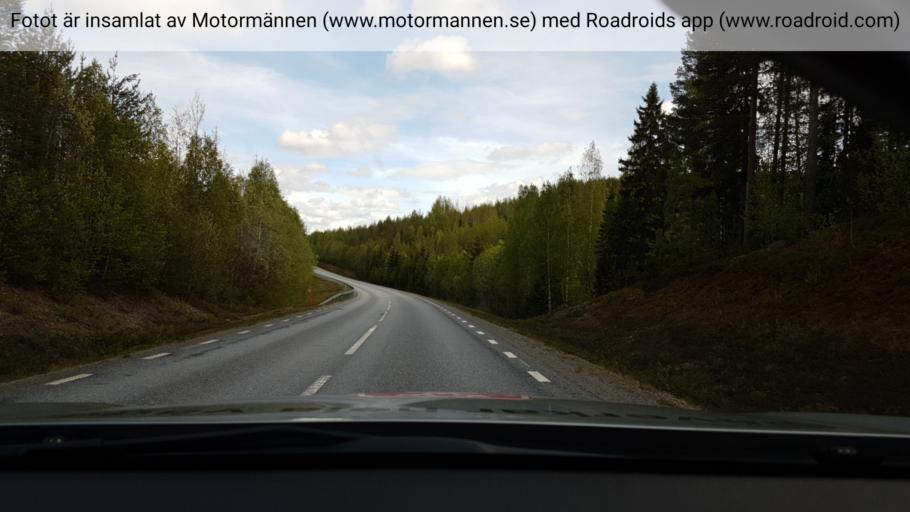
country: SE
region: Vaesterbotten
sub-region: Lycksele Kommun
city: Lycksele
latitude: 64.0408
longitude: 18.5847
